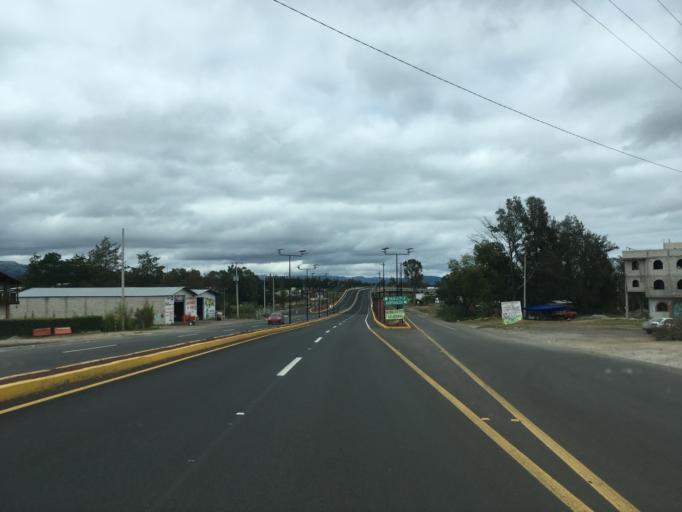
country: MX
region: Hidalgo
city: Atotonilco el Grande
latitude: 20.2969
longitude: -98.6735
